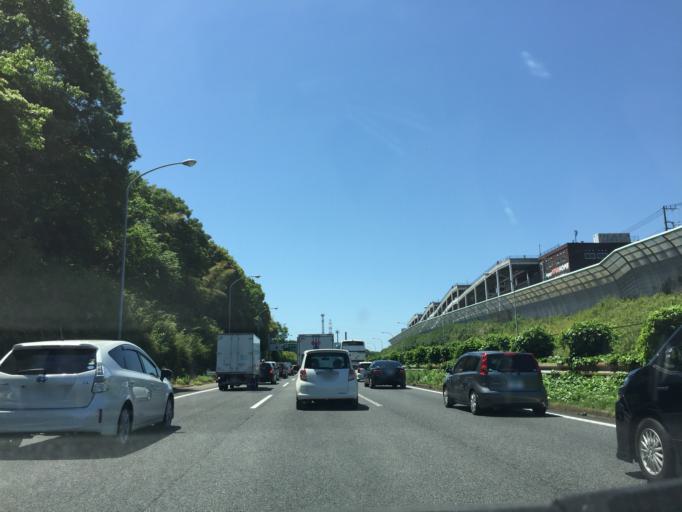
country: JP
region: Tokyo
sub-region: Machida-shi
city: Machida
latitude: 35.5212
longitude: 139.5039
